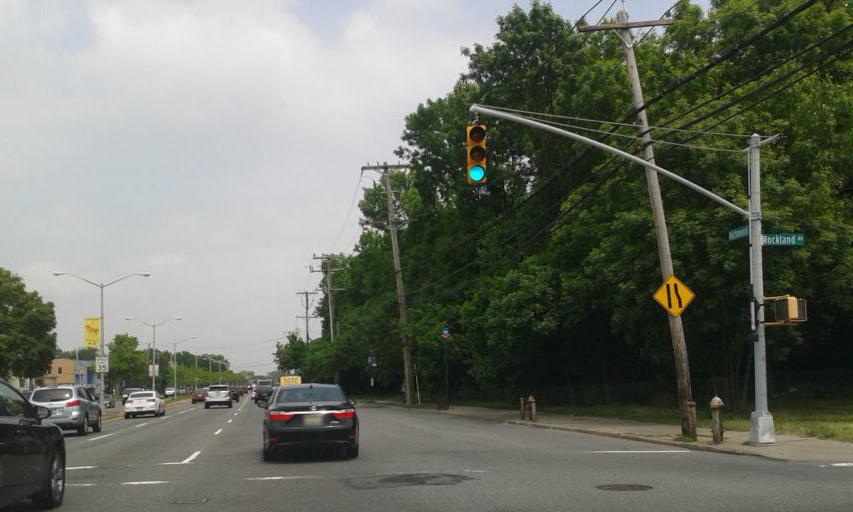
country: US
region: New York
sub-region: Richmond County
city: Bloomfield
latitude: 40.5951
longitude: -74.1618
